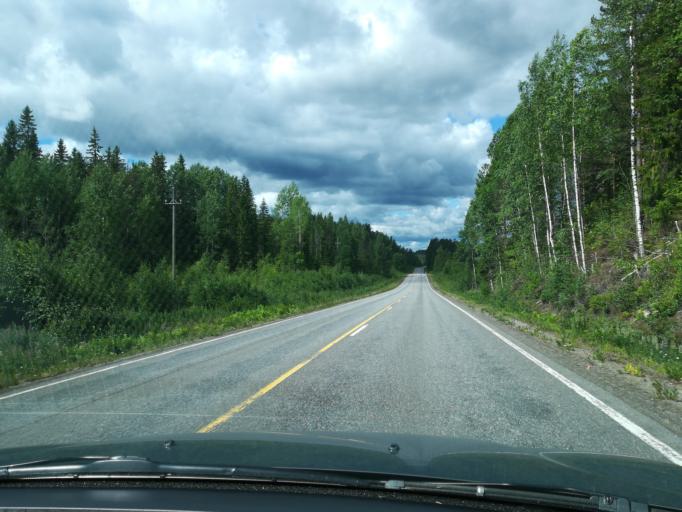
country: FI
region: Southern Savonia
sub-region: Mikkeli
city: Maentyharju
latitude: 61.3648
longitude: 26.9807
